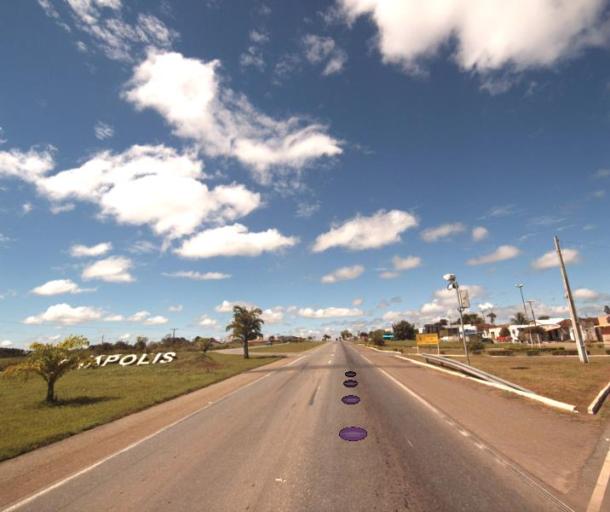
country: BR
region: Goias
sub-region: Rialma
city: Rialma
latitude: -15.4458
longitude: -49.5066
